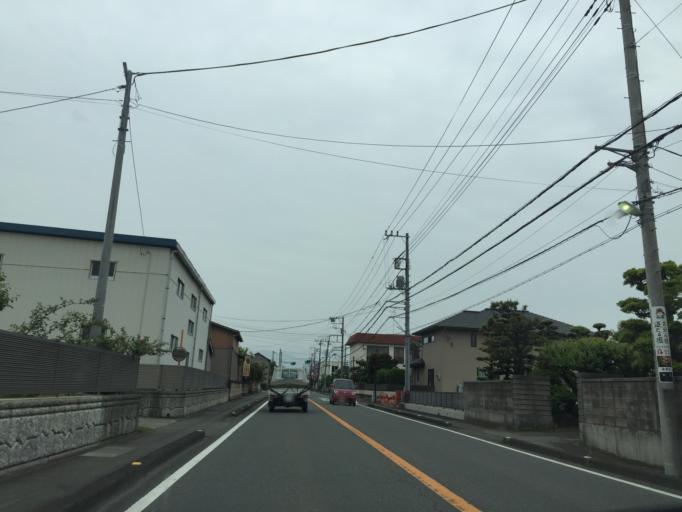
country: JP
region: Shizuoka
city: Mishima
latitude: 35.0702
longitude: 138.9420
